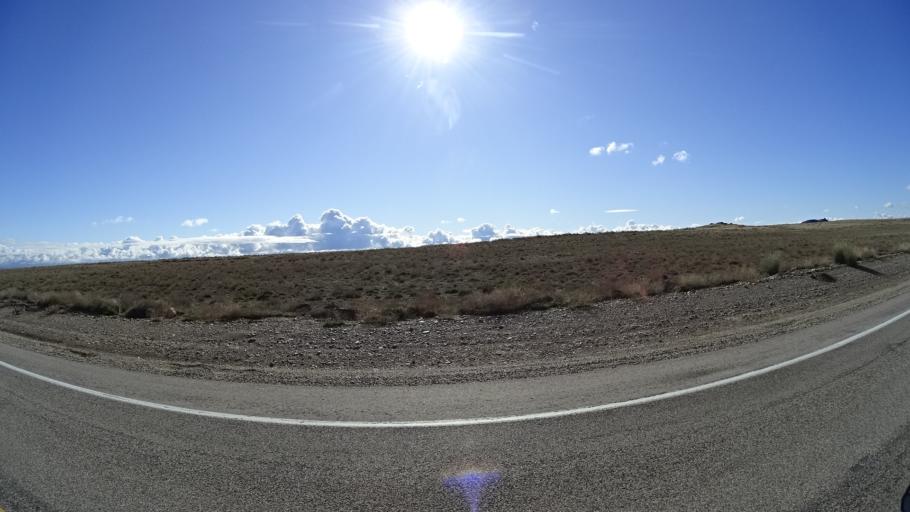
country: US
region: Idaho
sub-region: Ada County
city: Kuna
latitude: 43.3909
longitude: -116.4140
